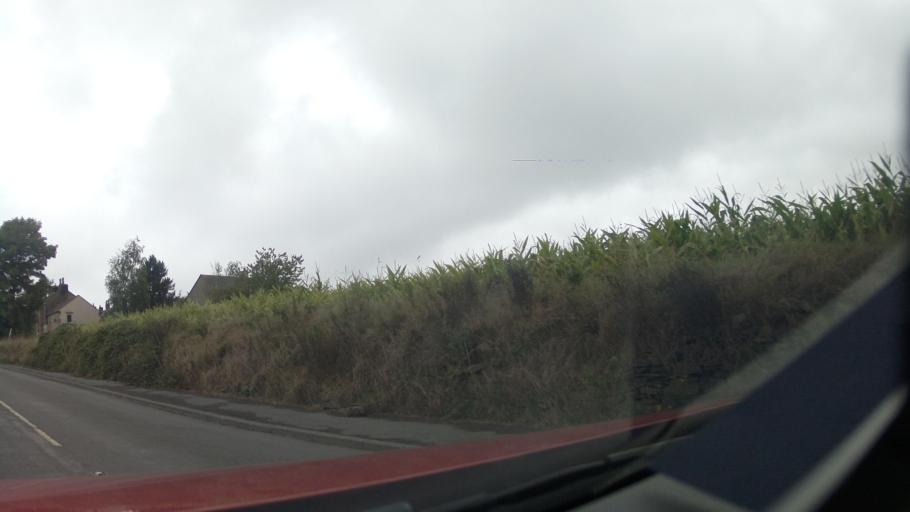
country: GB
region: England
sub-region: Kirklees
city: Clayton West
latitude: 53.6139
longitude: -1.6457
